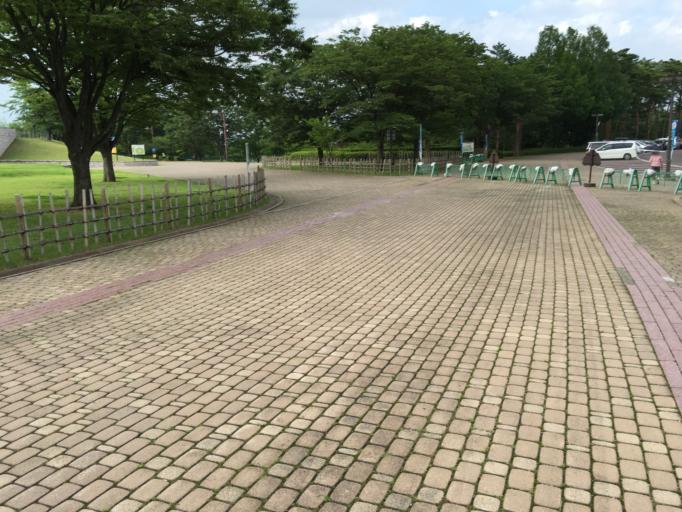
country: JP
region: Fukushima
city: Fukushima-shi
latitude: 37.7219
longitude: 140.3623
